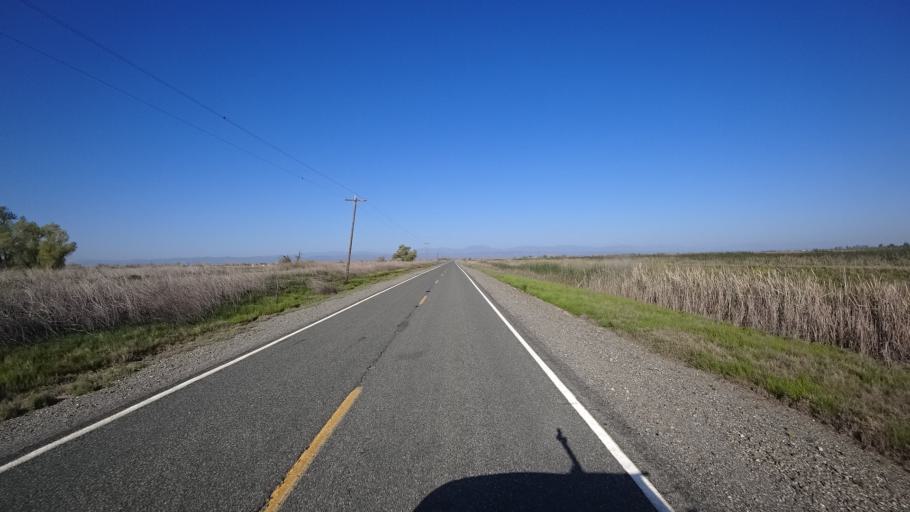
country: US
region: California
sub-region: Glenn County
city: Willows
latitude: 39.4073
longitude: -122.1672
